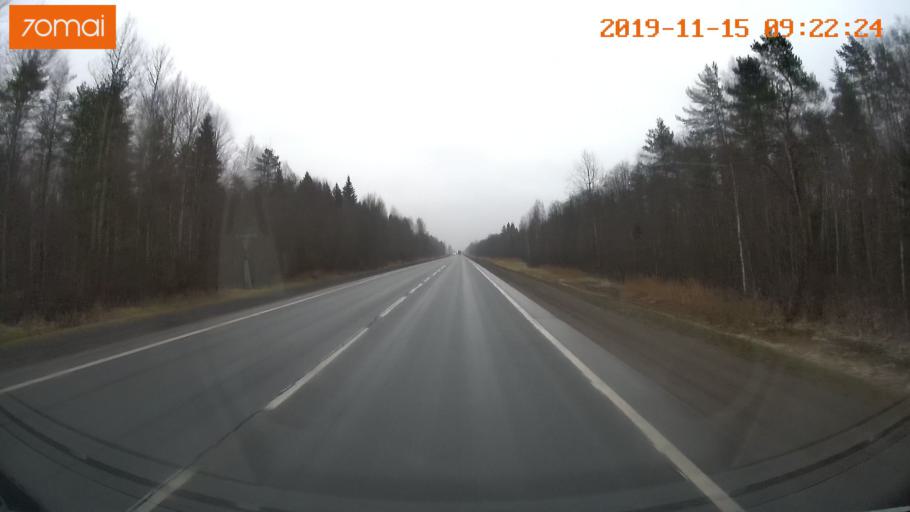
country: RU
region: Vologda
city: Tonshalovo
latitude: 59.2978
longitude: 38.0892
